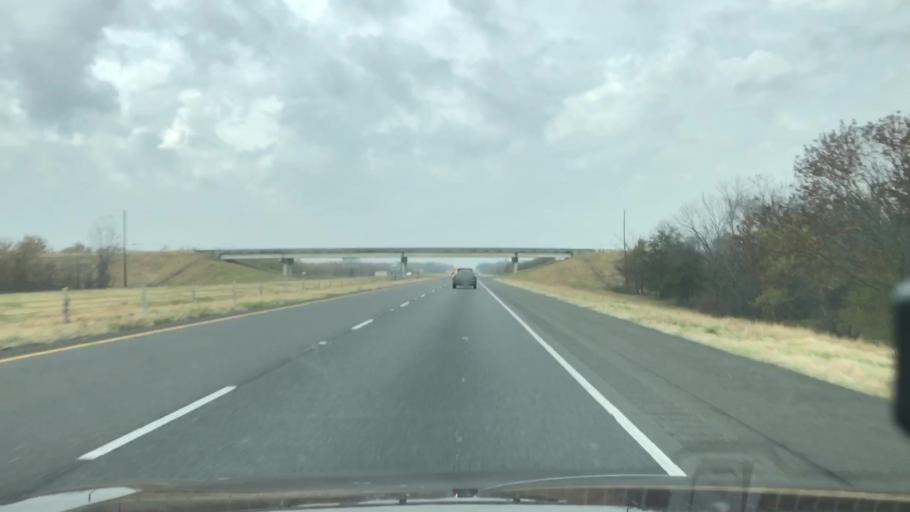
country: US
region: Louisiana
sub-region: Richland Parish
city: Delhi
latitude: 32.4371
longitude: -91.4560
